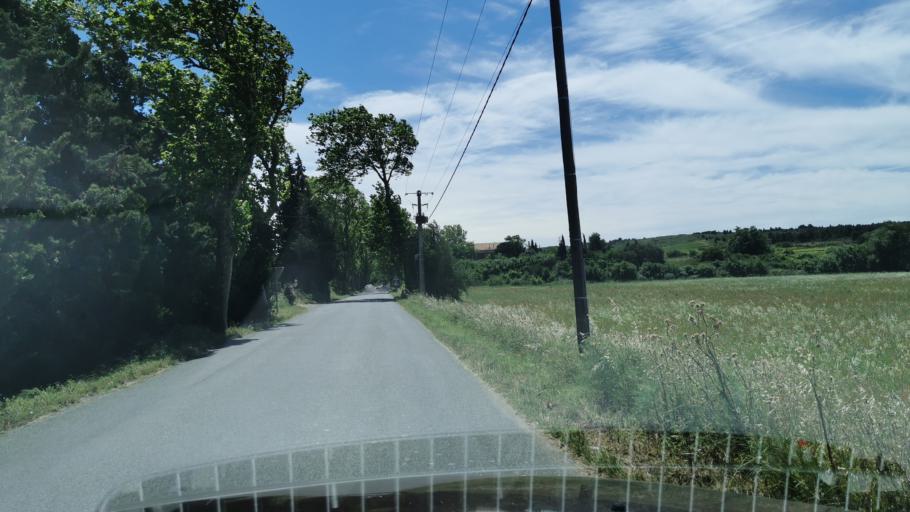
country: FR
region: Languedoc-Roussillon
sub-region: Departement de l'Aude
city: Marcorignan
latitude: 43.2163
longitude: 2.9283
